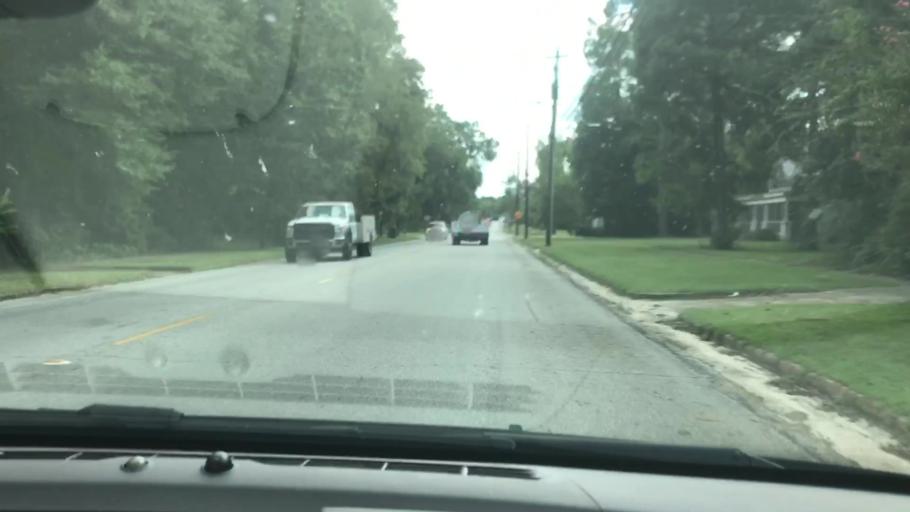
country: US
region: Georgia
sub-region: Clay County
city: Fort Gaines
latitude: 31.6098
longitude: -85.0498
